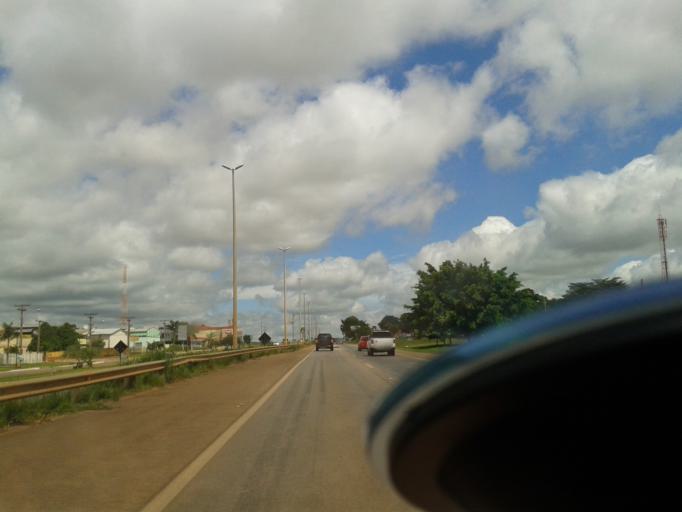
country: BR
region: Goias
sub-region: Goianira
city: Goianira
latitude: -16.5392
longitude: -49.4042
